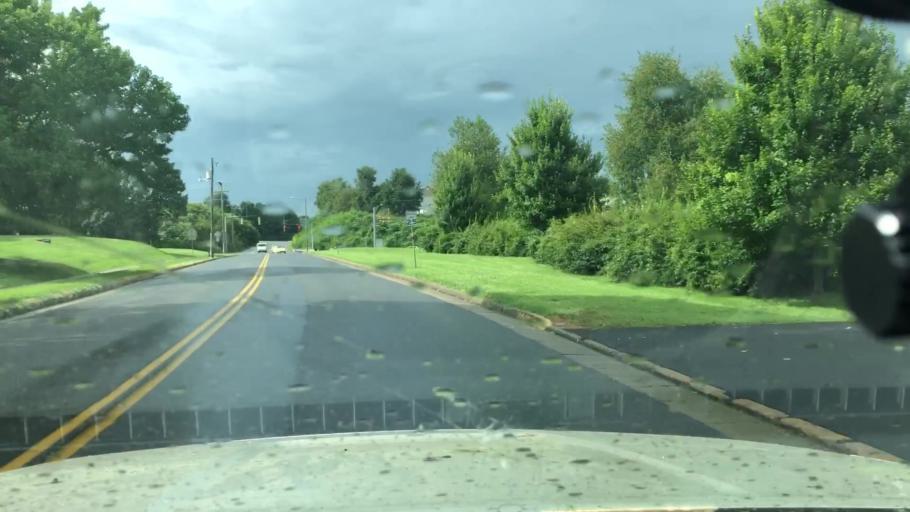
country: US
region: Virginia
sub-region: City of Waynesboro
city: Waynesboro
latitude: 38.0813
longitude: -78.8971
